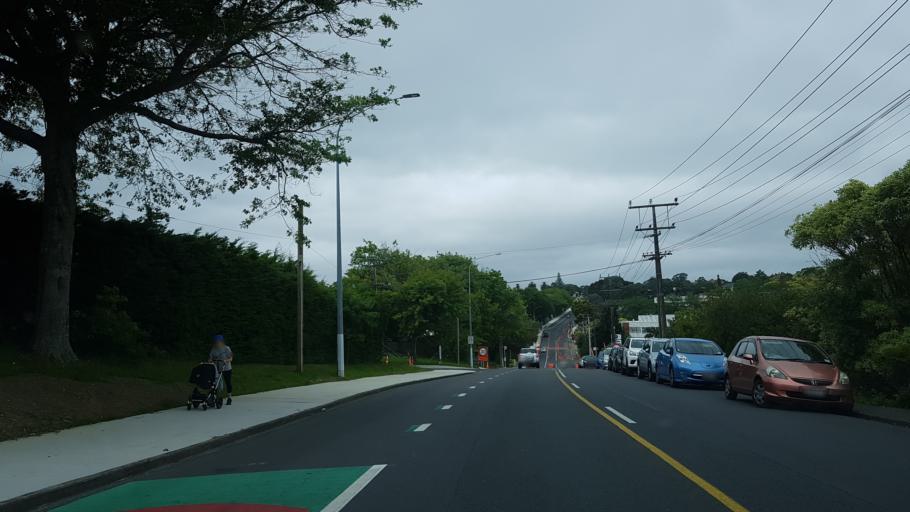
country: NZ
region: Auckland
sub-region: Auckland
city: North Shore
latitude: -36.8051
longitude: 174.7444
